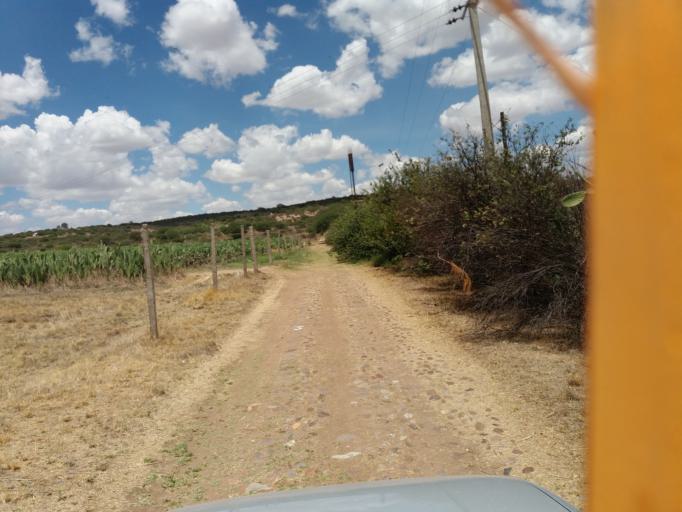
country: MX
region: Aguascalientes
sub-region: Aguascalientes
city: San Sebastian [Fraccionamiento]
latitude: 21.7734
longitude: -102.2641
